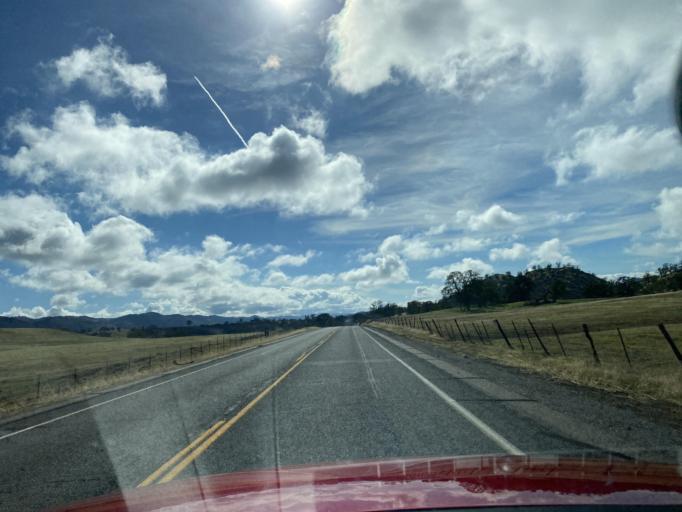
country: US
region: California
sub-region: Glenn County
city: Willows
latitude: 39.5273
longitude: -122.5318
